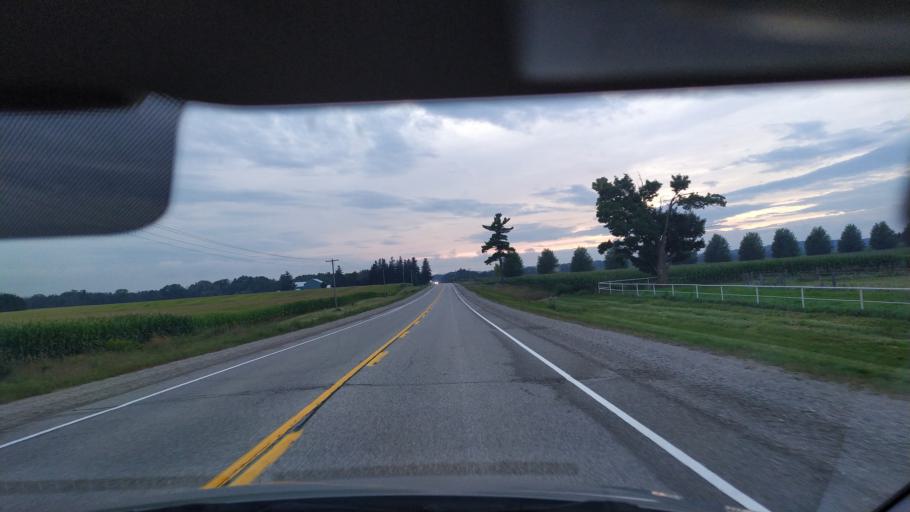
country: CA
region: Ontario
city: Kitchener
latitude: 43.3213
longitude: -80.5075
